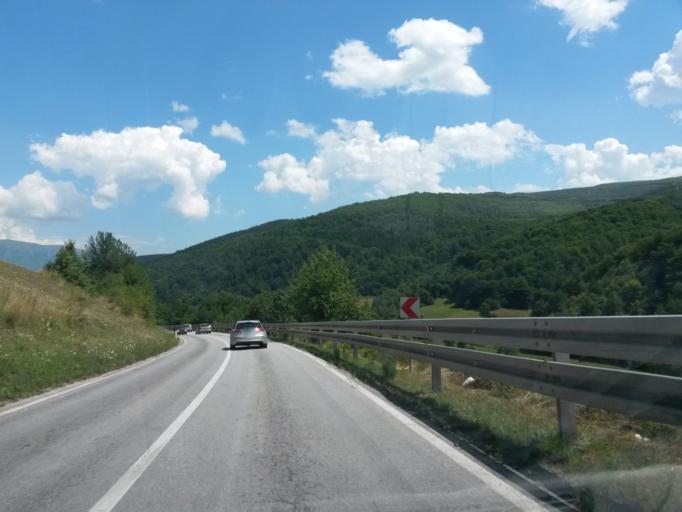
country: BA
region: Federation of Bosnia and Herzegovina
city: Turbe
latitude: 44.2090
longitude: 17.5203
